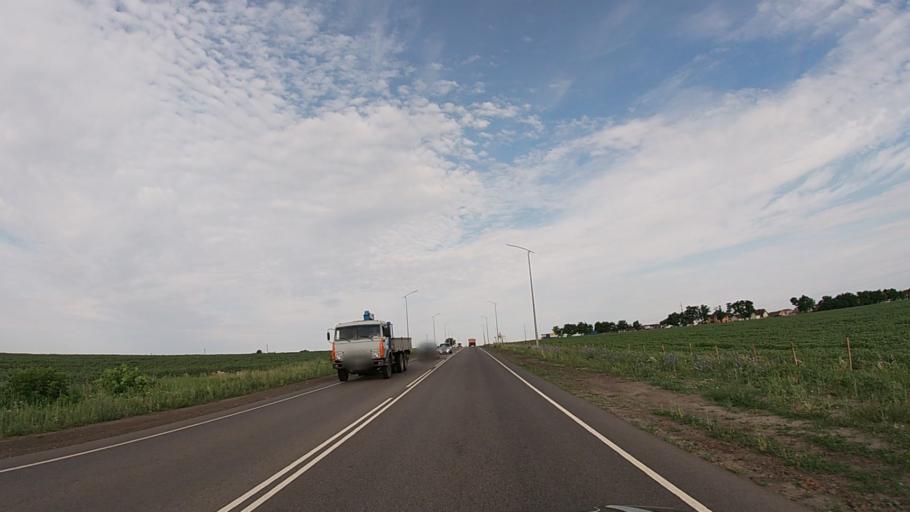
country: RU
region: Belgorod
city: Severnyy
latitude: 50.6650
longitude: 36.5069
